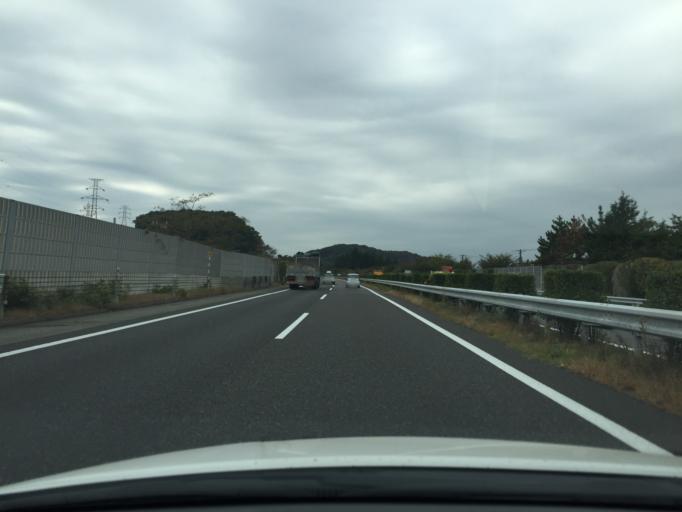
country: JP
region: Tochigi
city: Kuroiso
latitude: 37.1358
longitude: 140.1890
